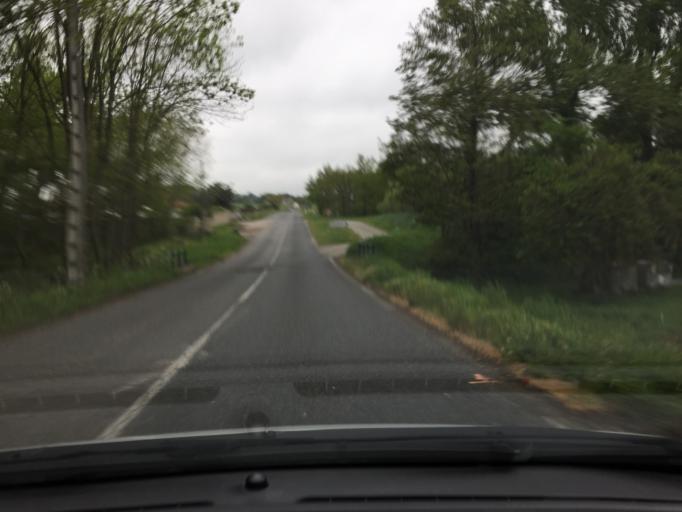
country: FR
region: Rhone-Alpes
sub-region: Departement du Rhone
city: Mornant
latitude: 45.6147
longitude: 4.7012
